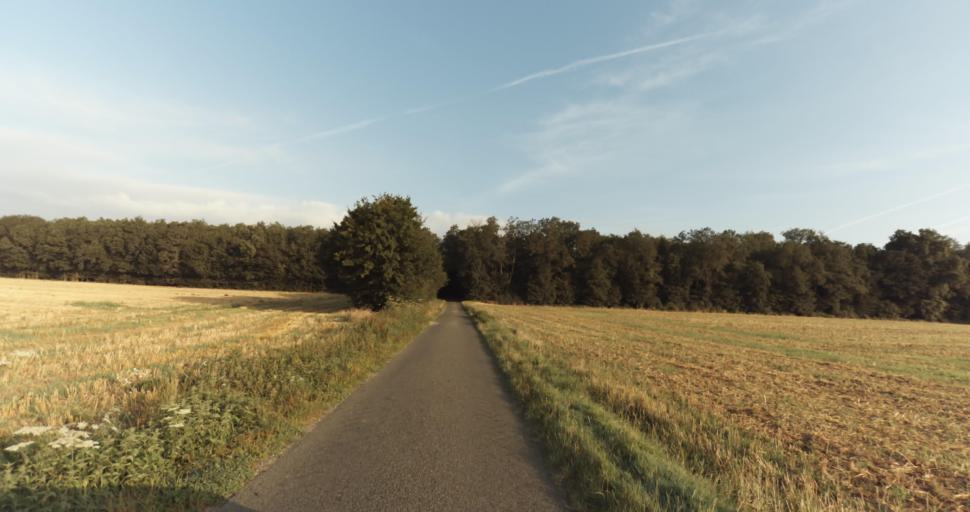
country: FR
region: Centre
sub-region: Departement d'Eure-et-Loir
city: Vert-en-Drouais
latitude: 48.7745
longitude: 1.3226
